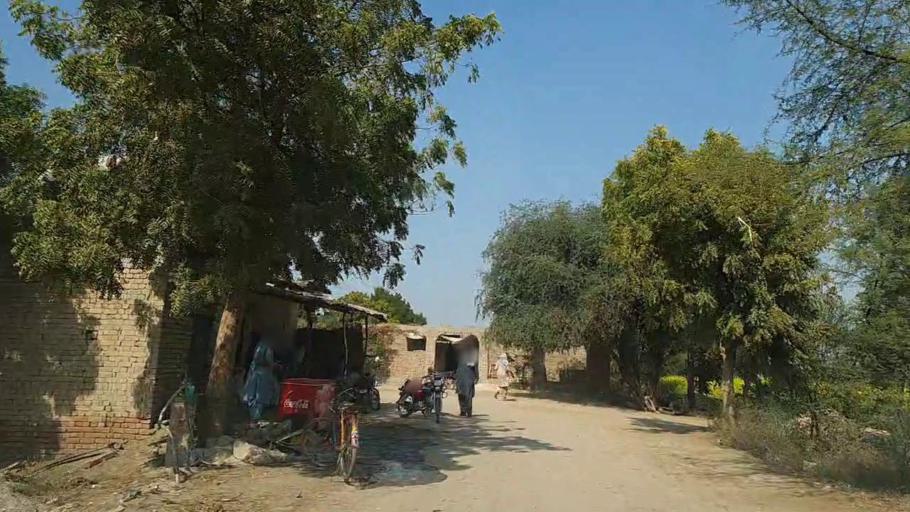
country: PK
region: Sindh
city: Daur
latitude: 26.4993
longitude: 68.2719
